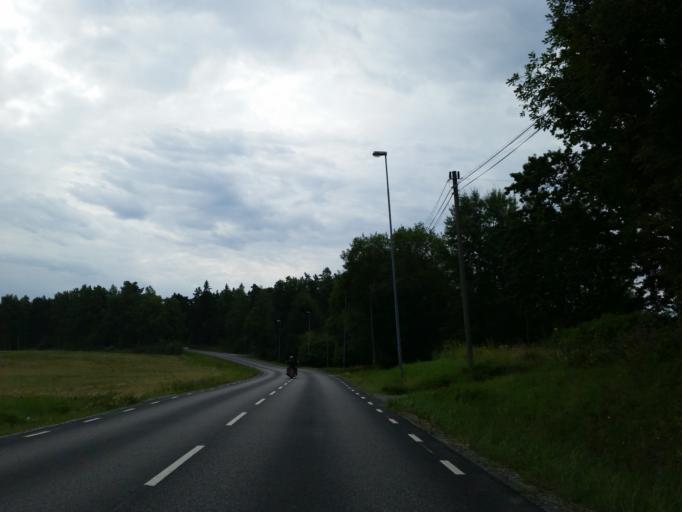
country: SE
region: Stockholm
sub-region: Botkyrka Kommun
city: Eriksberg
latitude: 59.2356
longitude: 17.7813
